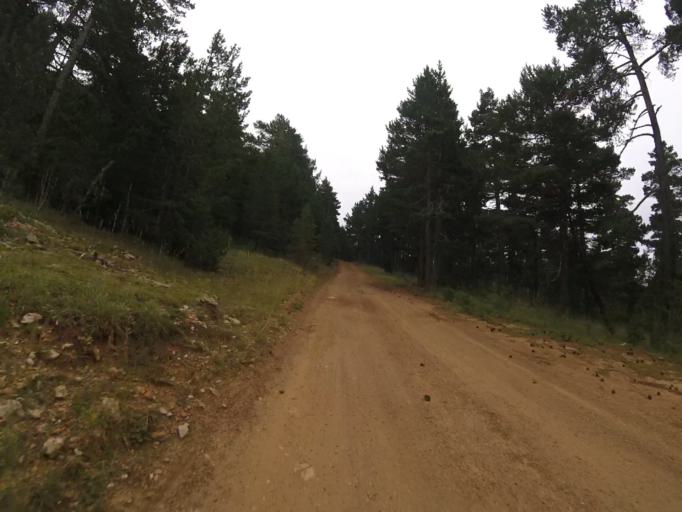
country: ES
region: Aragon
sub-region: Provincia de Teruel
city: Valdelinares
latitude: 40.3678
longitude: -0.6189
